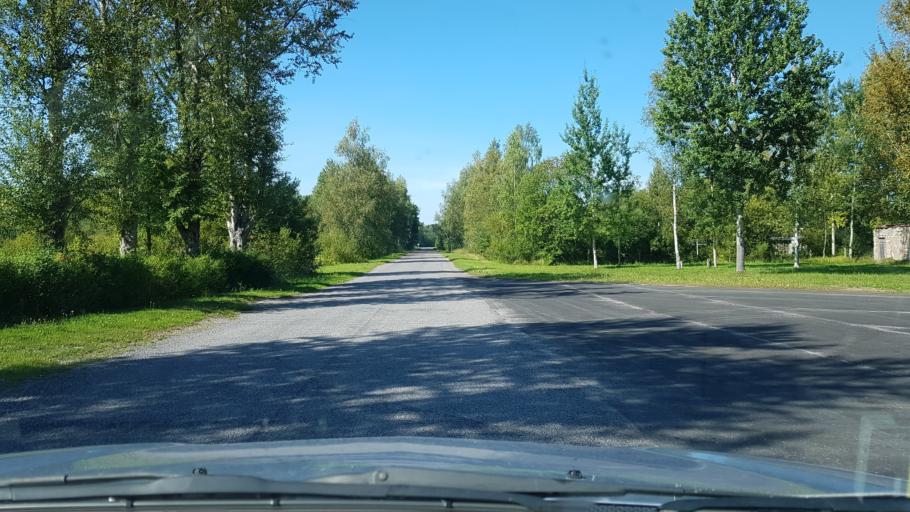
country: EE
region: Ida-Virumaa
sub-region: Sillamaee linn
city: Sillamae
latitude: 59.3203
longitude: 27.7804
